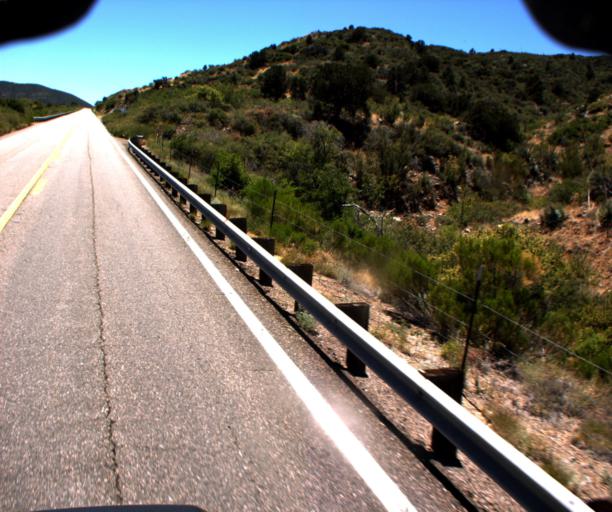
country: US
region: Arizona
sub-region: Gila County
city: Globe
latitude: 33.2853
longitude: -110.7518
